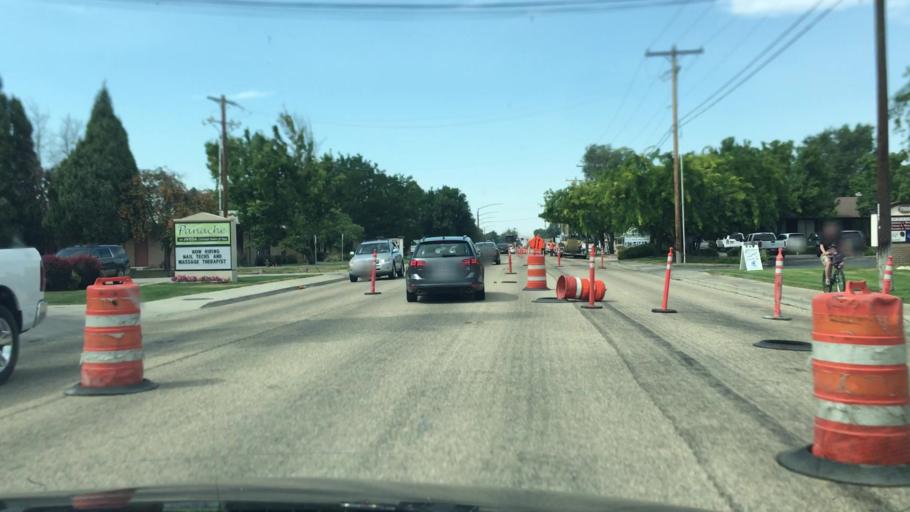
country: US
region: Idaho
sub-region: Ada County
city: Garden City
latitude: 43.6150
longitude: -116.2742
